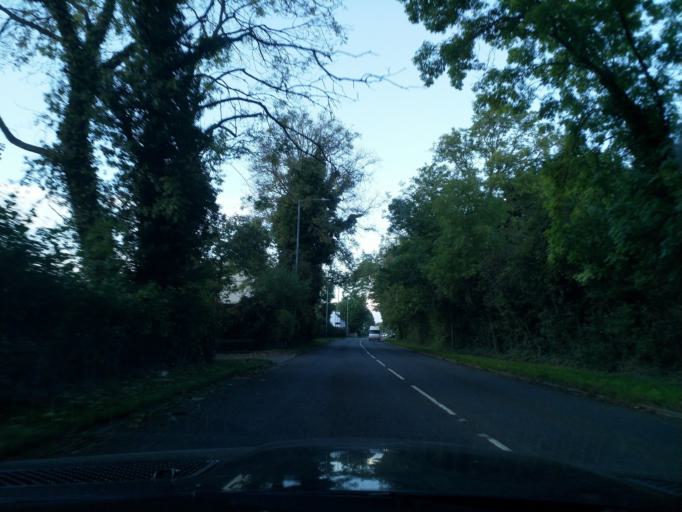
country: GB
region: England
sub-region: Warwickshire
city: Henley in Arden
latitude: 52.3418
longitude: -1.7752
